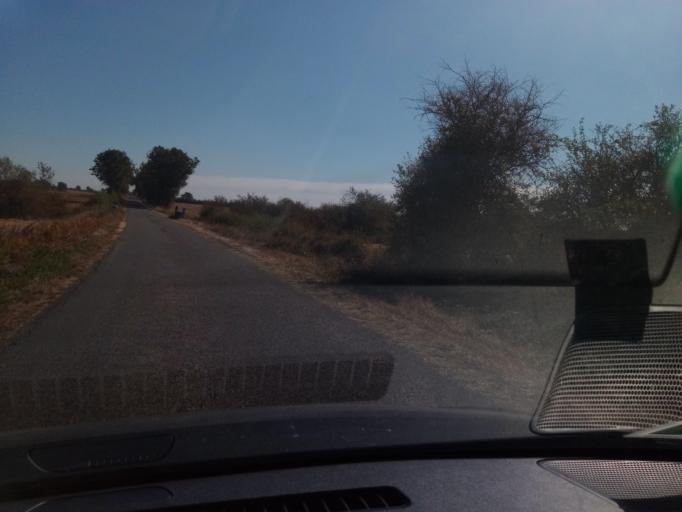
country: FR
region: Poitou-Charentes
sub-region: Departement de la Vienne
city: Saulge
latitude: 46.3784
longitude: 0.7988
